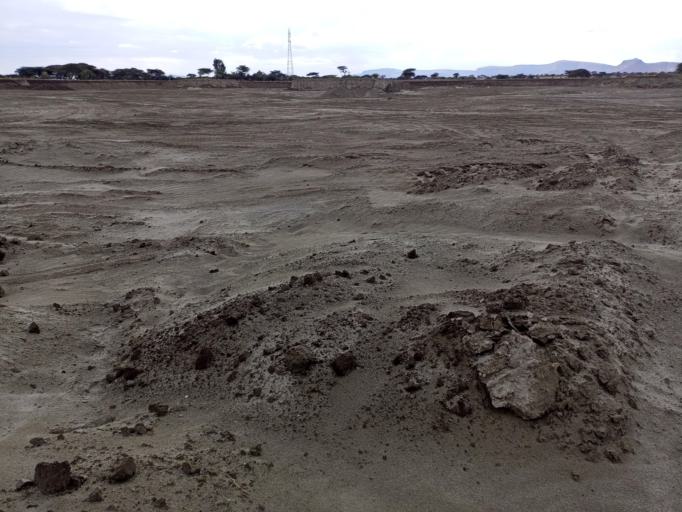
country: ET
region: Oromiya
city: Ziway
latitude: 7.9213
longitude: 38.6822
